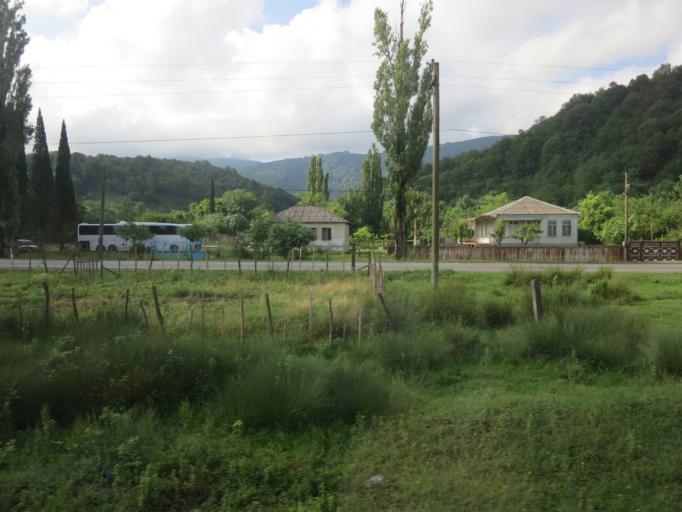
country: GE
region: Samegrelo and Zemo Svaneti
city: Abasha
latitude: 42.0966
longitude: 42.1991
